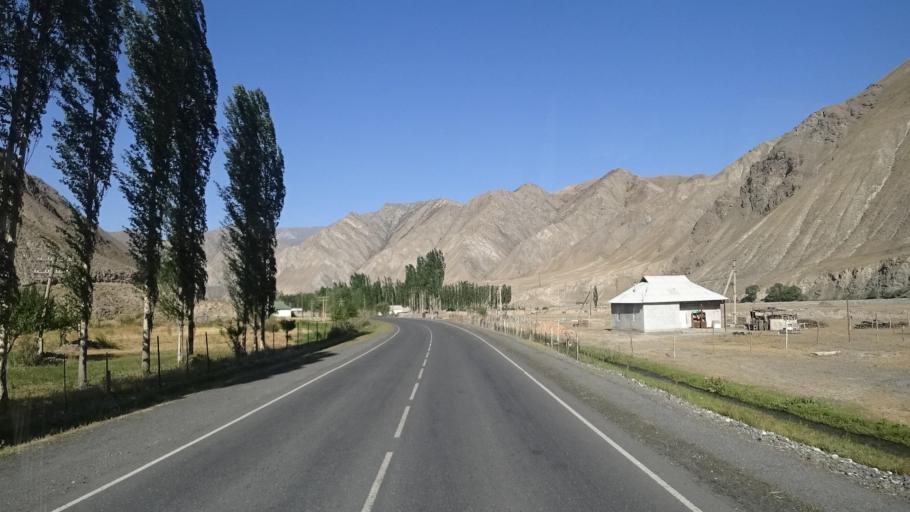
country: KG
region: Osh
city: Gul'cha
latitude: 40.0326
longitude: 73.5235
